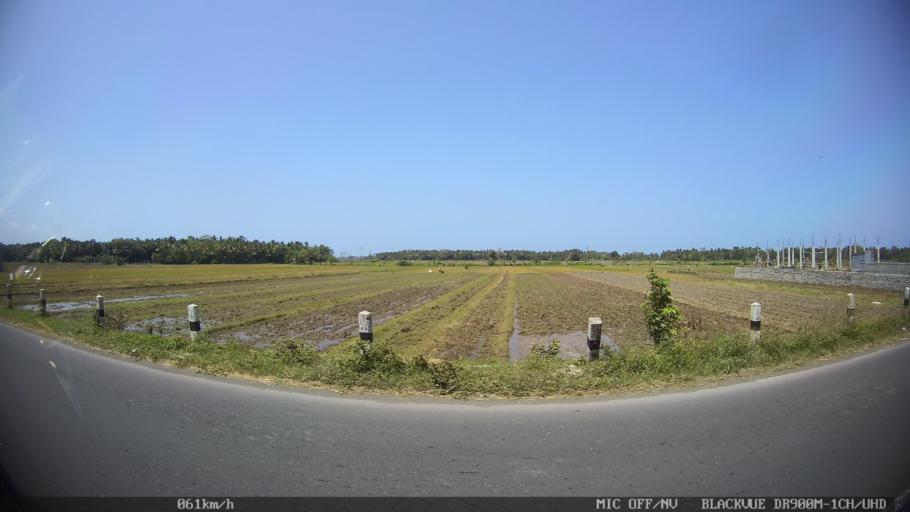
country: ID
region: Daerah Istimewa Yogyakarta
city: Srandakan
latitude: -7.9525
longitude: 110.1983
